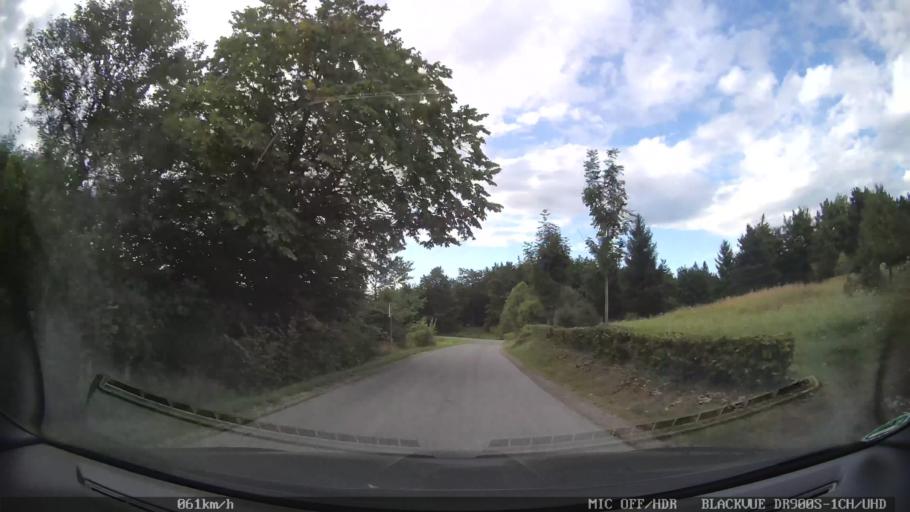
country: HR
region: Licko-Senjska
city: Jezerce
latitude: 44.9435
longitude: 15.5414
